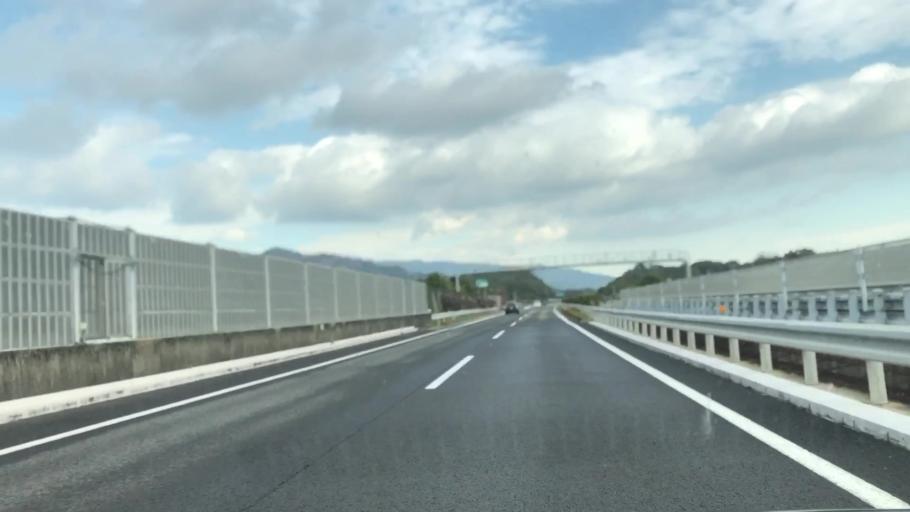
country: JP
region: Saga Prefecture
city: Kanzakimachi-kanzaki
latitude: 33.3467
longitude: 130.3669
